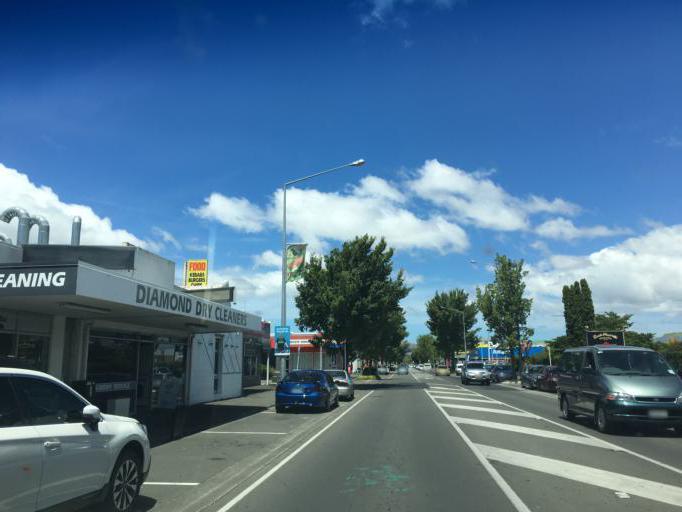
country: NZ
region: Hawke's Bay
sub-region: Hastings District
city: Hastings
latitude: -39.6347
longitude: 176.8356
